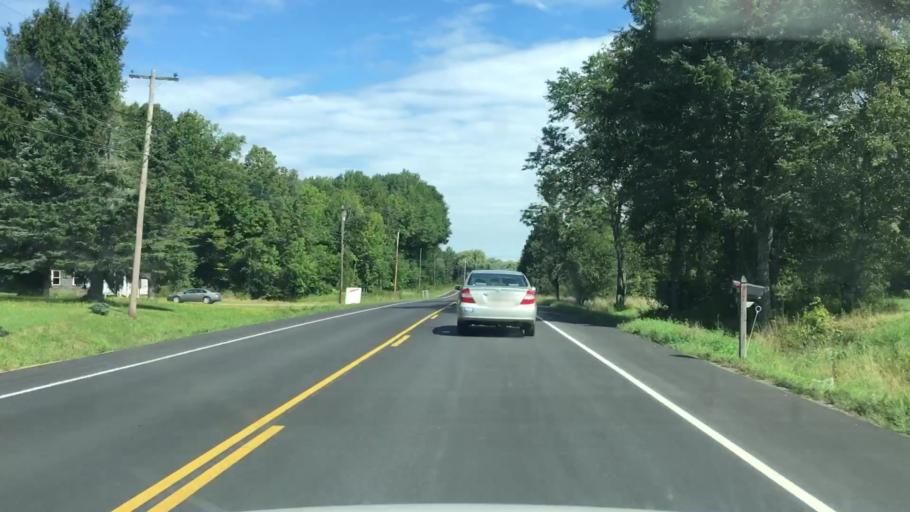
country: US
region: Maine
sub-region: Penobscot County
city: Corinna
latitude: 44.9396
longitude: -69.2482
